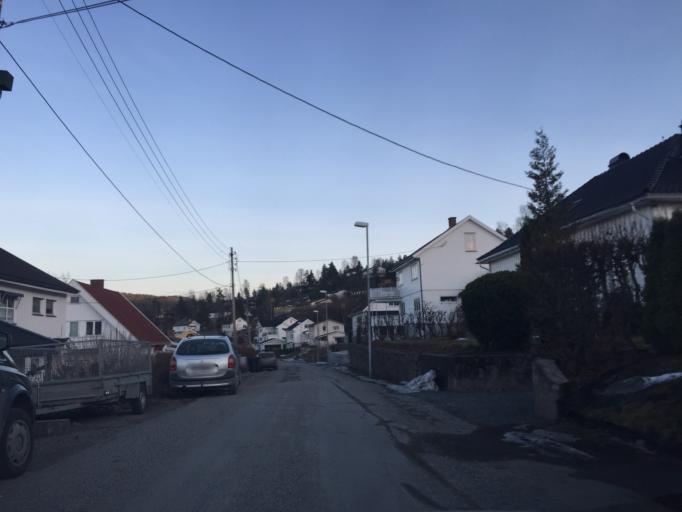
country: NO
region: Buskerud
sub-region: Drammen
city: Drammen
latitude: 59.7275
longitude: 10.2066
